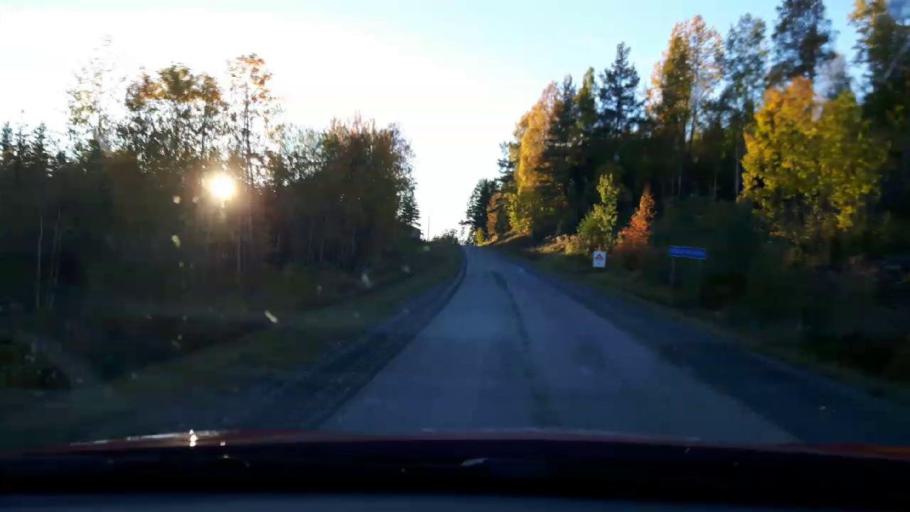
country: SE
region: Jaemtland
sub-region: Krokoms Kommun
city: Krokom
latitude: 63.4250
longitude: 14.4724
